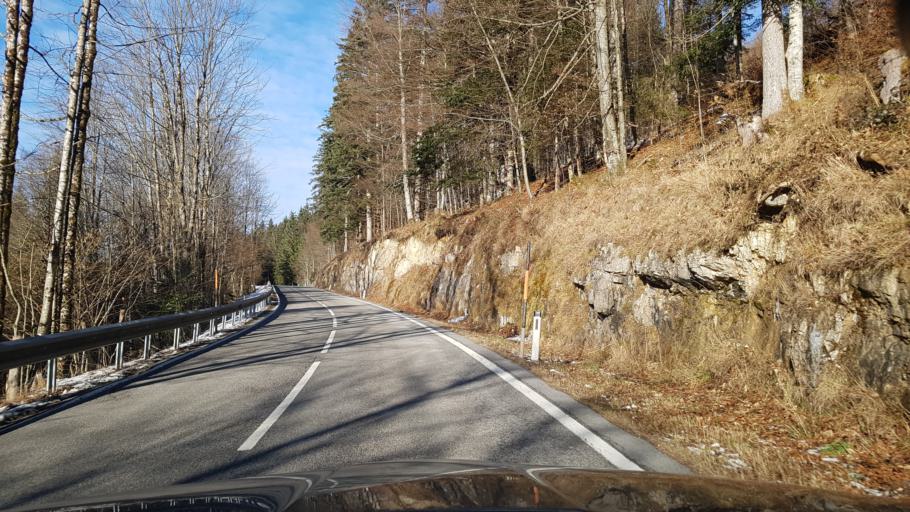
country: AT
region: Salzburg
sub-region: Politischer Bezirk Salzburg-Umgebung
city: Faistenau
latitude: 47.7514
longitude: 13.2526
